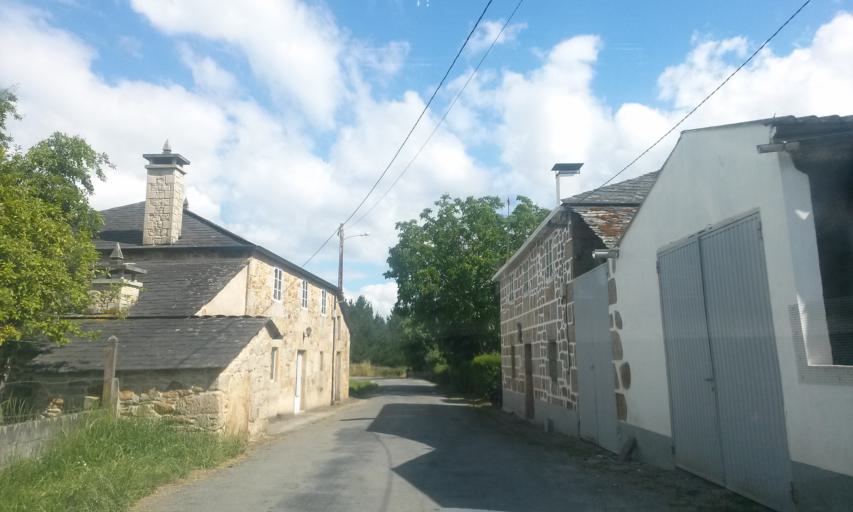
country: ES
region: Galicia
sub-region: Provincia de Lugo
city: Begonte
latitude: 43.1182
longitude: -7.6720
